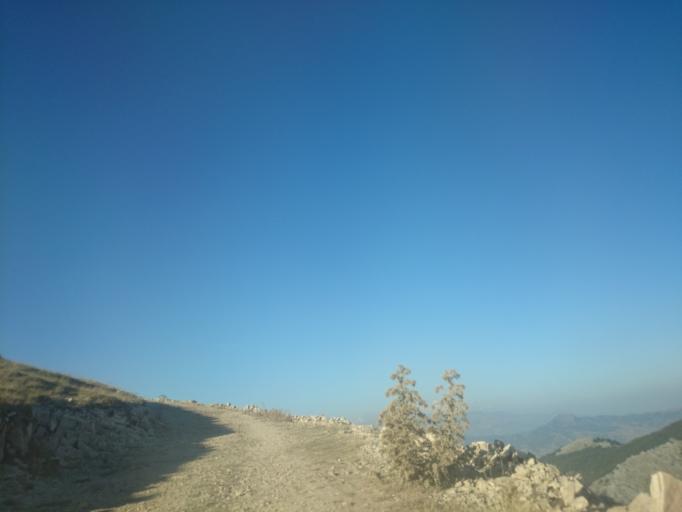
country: AL
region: Berat
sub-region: Rrethi i Skraparit
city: Bogove
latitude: 40.6114
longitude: 20.1884
